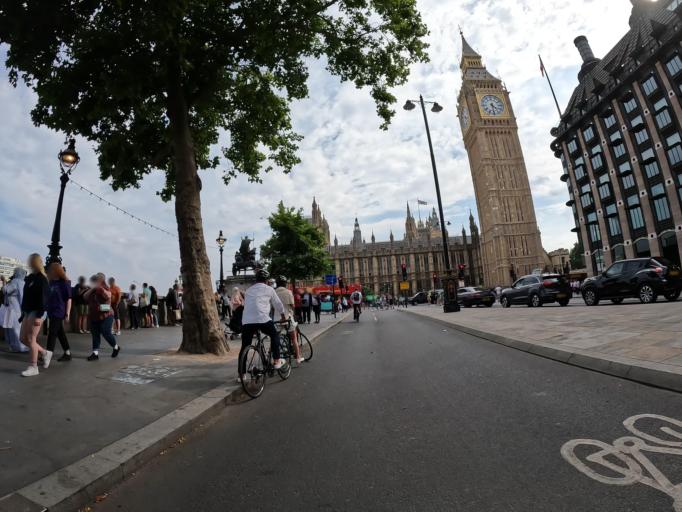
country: GB
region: England
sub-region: Greater London
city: Orpington
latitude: 51.3459
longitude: 0.0959
